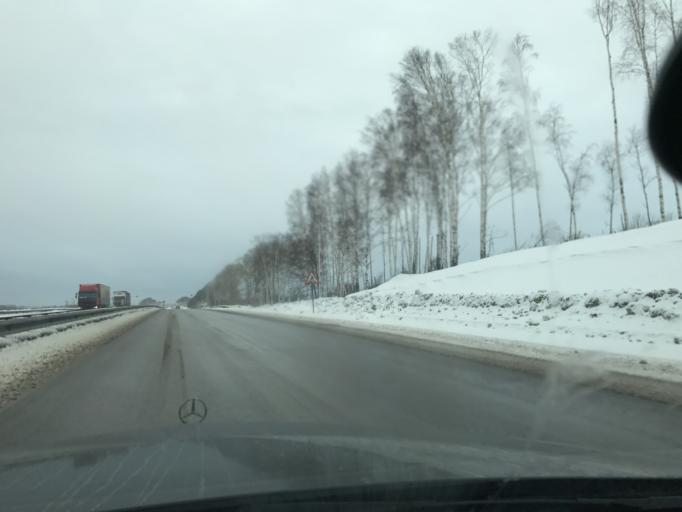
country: RU
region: Vladimir
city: Gorokhovets
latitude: 56.1600
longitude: 42.5619
